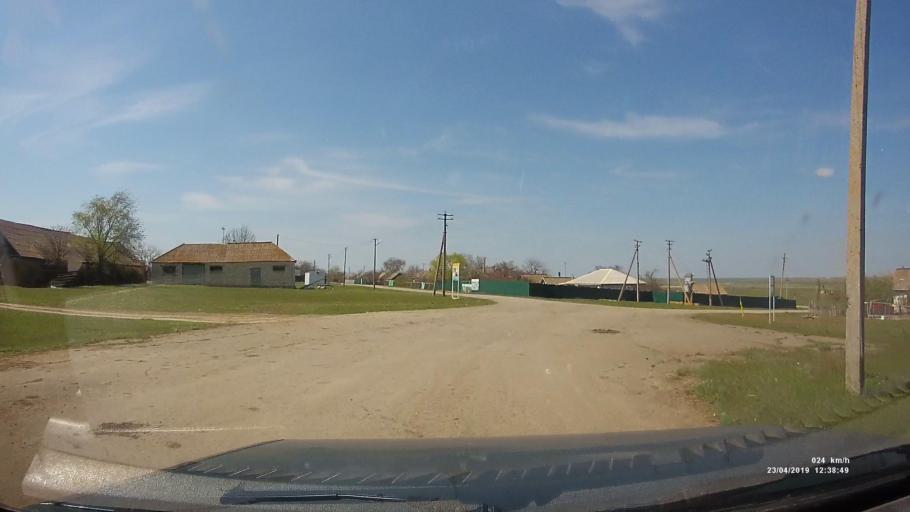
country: RU
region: Kalmykiya
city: Yashalta
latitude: 46.4330
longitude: 42.7117
